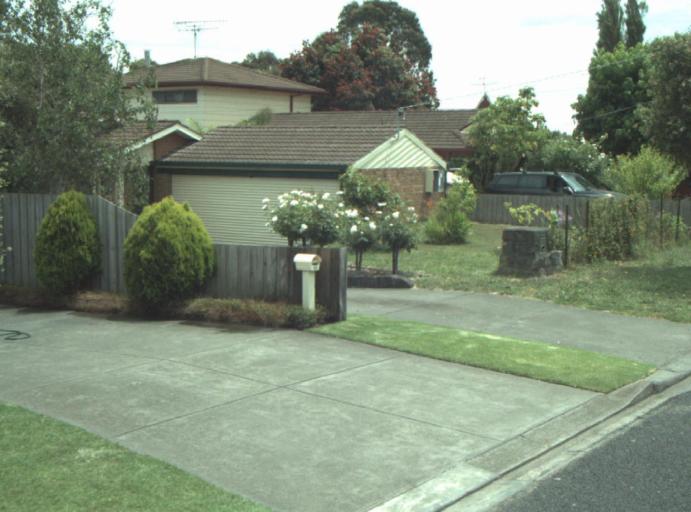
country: AU
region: Victoria
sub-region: Greater Geelong
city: Clifton Springs
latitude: -38.1609
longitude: 144.5519
